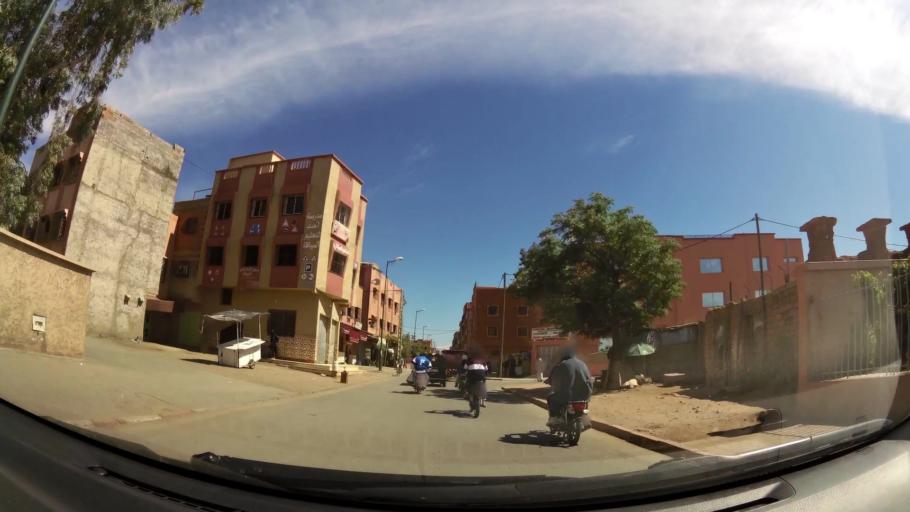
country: MA
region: Marrakech-Tensift-Al Haouz
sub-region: Marrakech
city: Marrakesh
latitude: 31.5999
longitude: -7.9614
